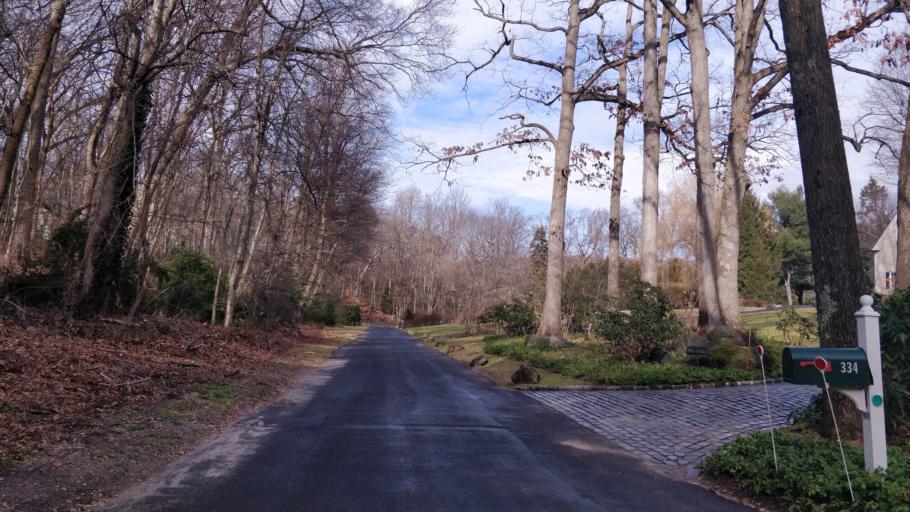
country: US
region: New York
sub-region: Nassau County
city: Oyster Bay
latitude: 40.8735
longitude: -73.5556
